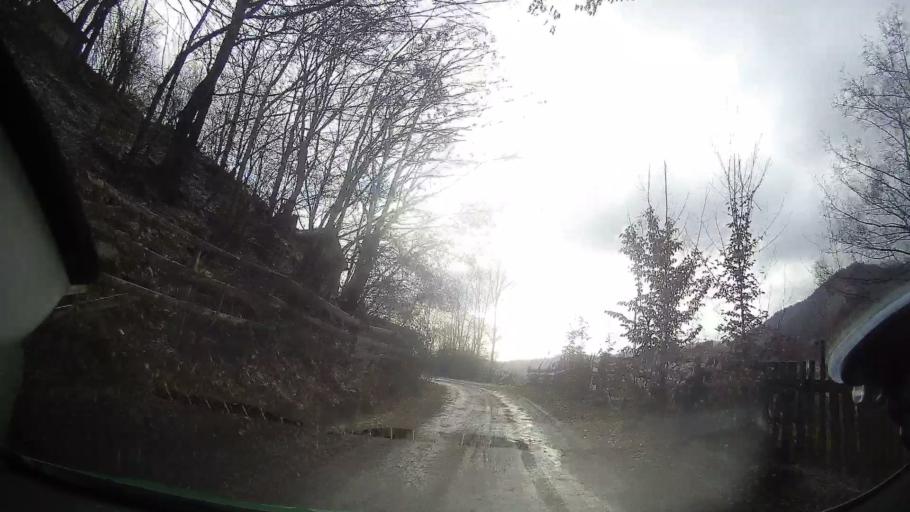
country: RO
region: Cluj
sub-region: Comuna Valea Ierii
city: Valea Ierii
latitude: 46.6488
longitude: 23.3500
